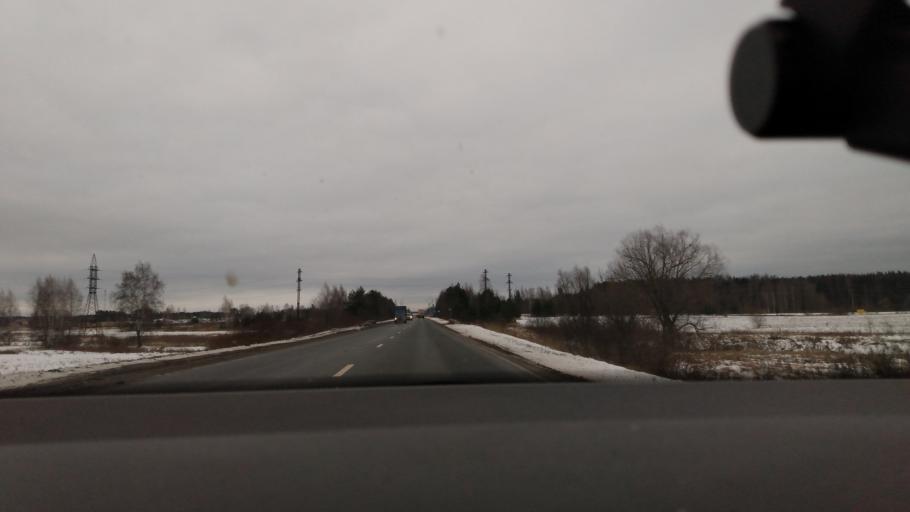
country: RU
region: Moskovskaya
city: Yegor'yevsk
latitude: 55.4229
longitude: 39.0382
